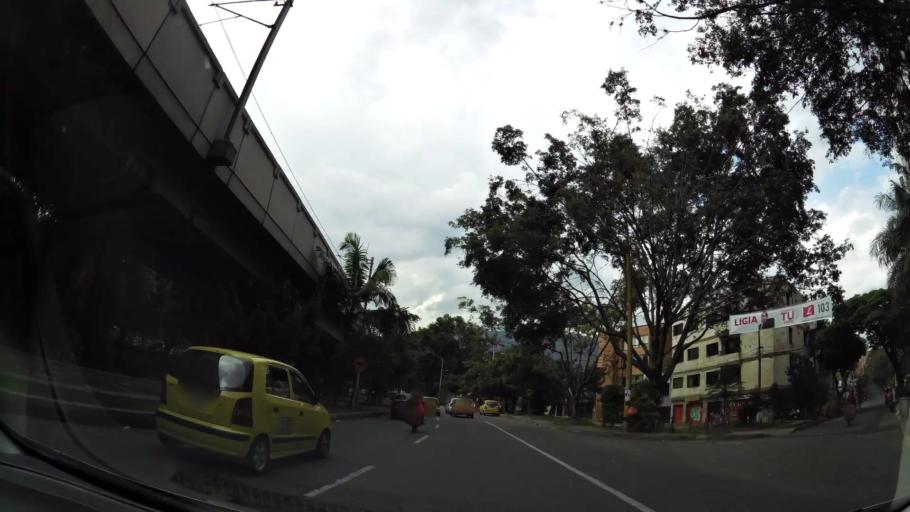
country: CO
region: Antioquia
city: Medellin
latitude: 6.2568
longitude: -75.5926
